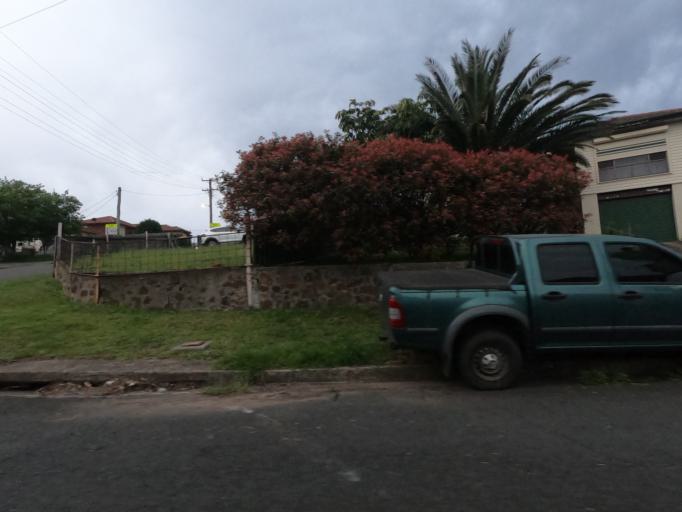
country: AU
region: New South Wales
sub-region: Wollongong
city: Lake Heights
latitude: -34.4812
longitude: 150.8714
